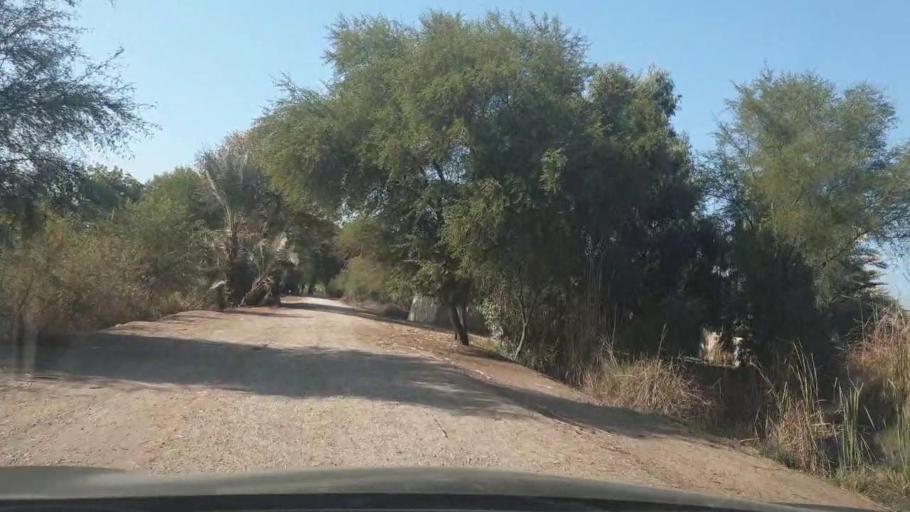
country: PK
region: Sindh
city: Khairpur
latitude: 28.1442
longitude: 69.5972
